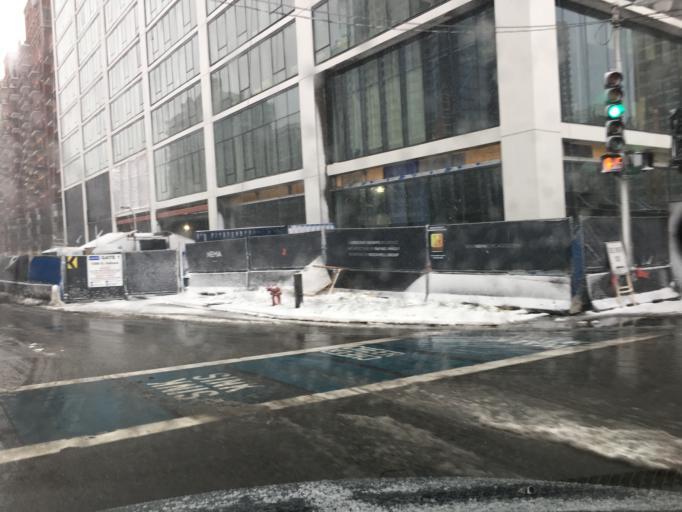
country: US
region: Illinois
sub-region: Cook County
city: Chicago
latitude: 41.8685
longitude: -87.6228
